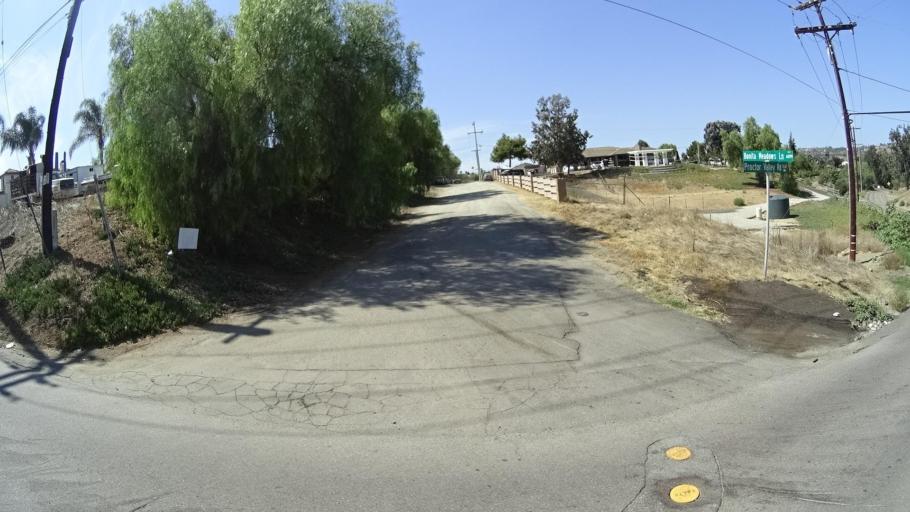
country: US
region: California
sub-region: San Diego County
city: La Presa
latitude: 32.6765
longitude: -116.9989
